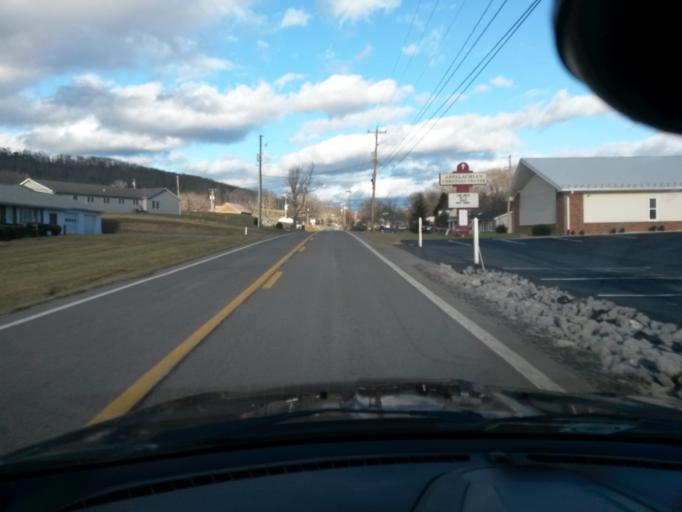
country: US
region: Virginia
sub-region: Giles County
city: Pearisburg
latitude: 37.4072
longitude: -80.7571
